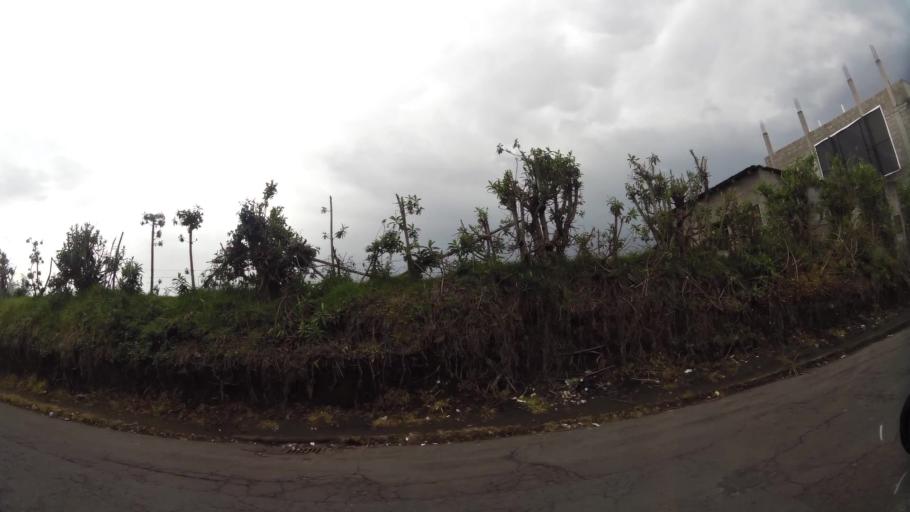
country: EC
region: Pichincha
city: Sangolqui
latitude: -0.3544
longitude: -78.5516
